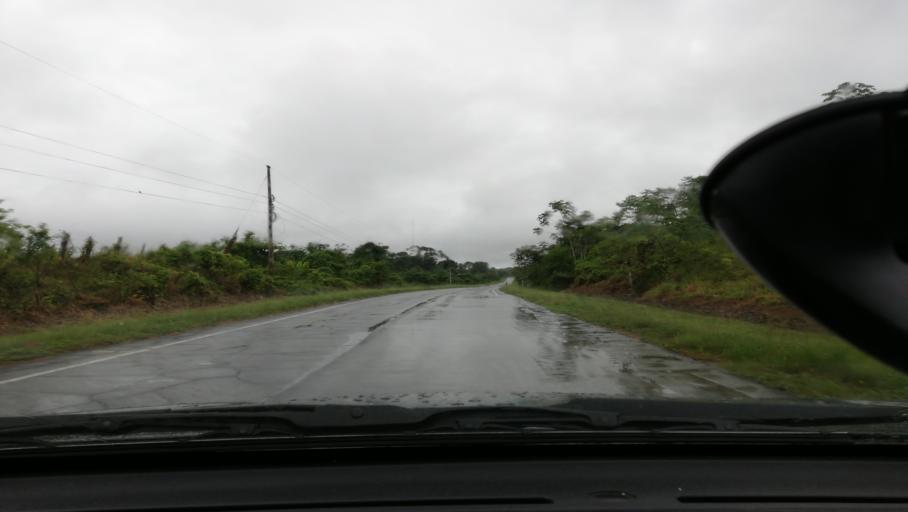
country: PE
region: Loreto
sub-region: Provincia de Maynas
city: San Juan
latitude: -4.1629
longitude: -73.4741
